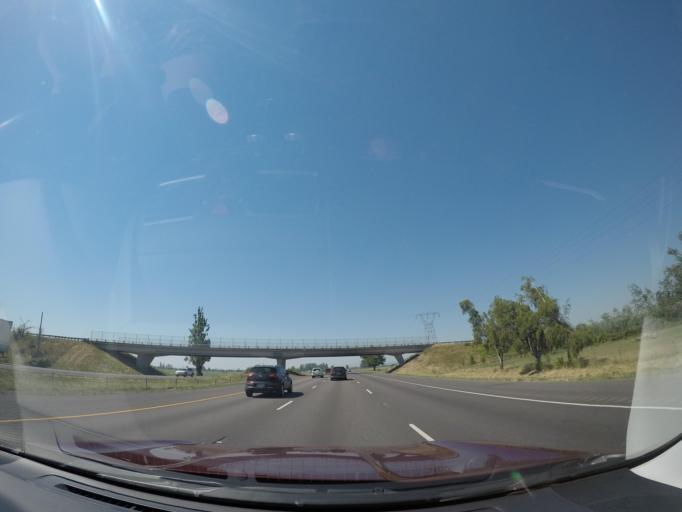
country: US
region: Oregon
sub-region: Marion County
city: Gervais
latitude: 45.1011
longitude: -122.9317
